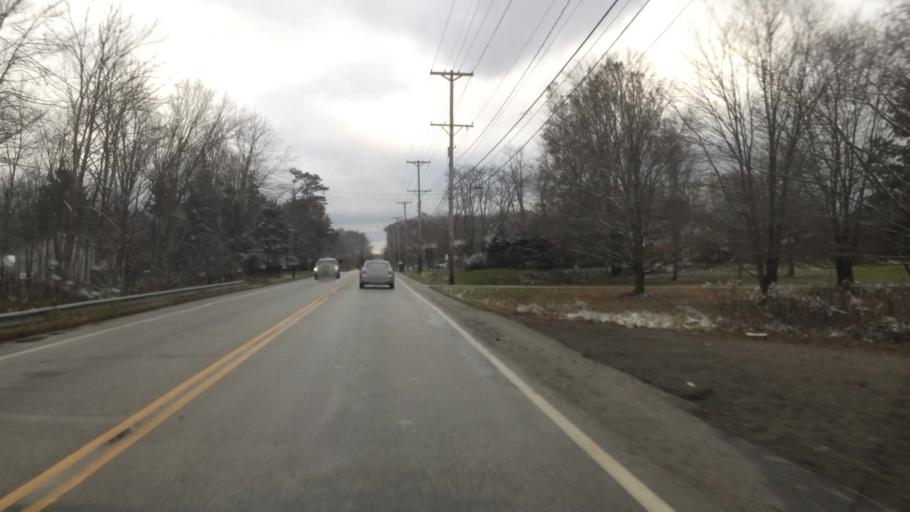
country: US
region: Ohio
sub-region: Summit County
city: Hudson
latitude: 41.2218
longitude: -81.4112
